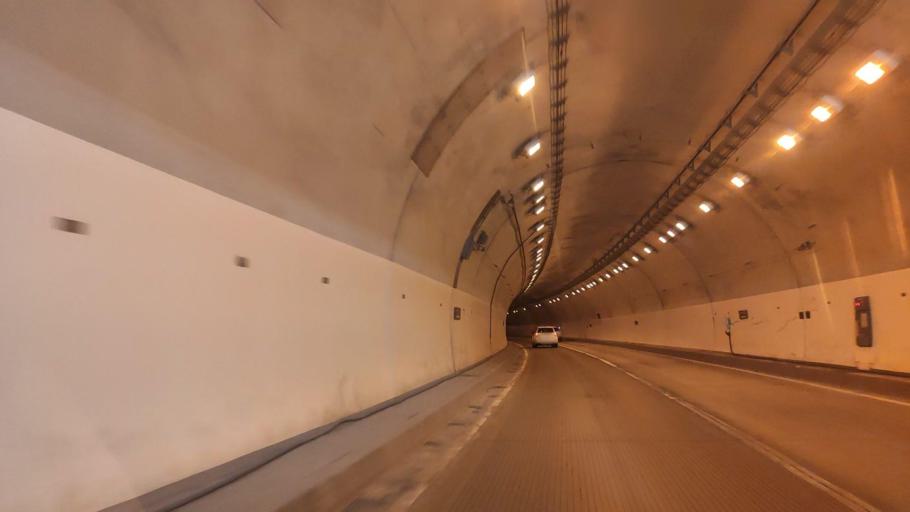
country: JP
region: Hokkaido
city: Ishikari
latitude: 43.4692
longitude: 141.3973
